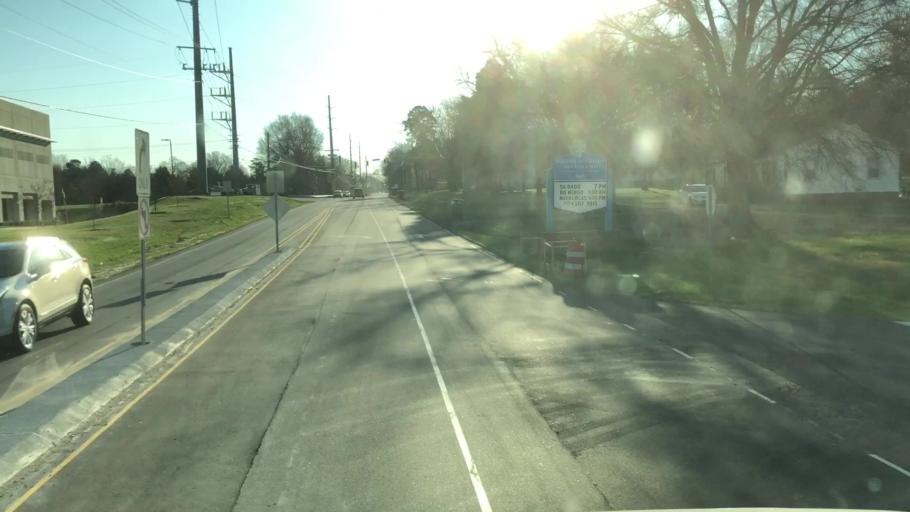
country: US
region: North Carolina
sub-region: Cabarrus County
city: Concord
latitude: 35.4148
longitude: -80.6559
